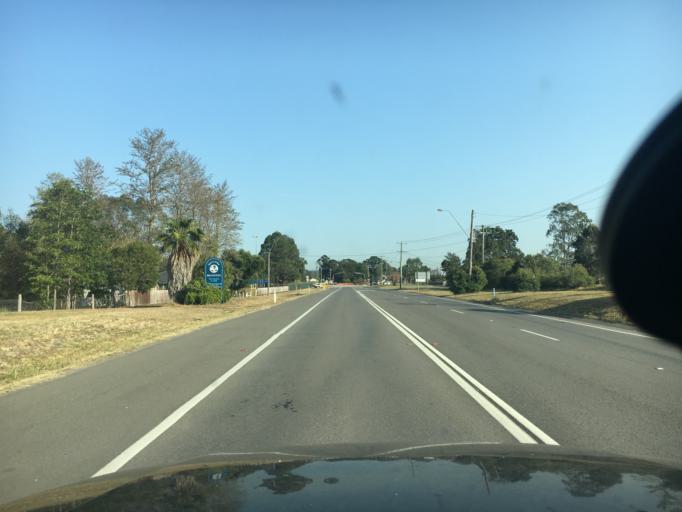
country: AU
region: New South Wales
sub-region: Cessnock
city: Branxton
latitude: -32.6591
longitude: 151.3636
